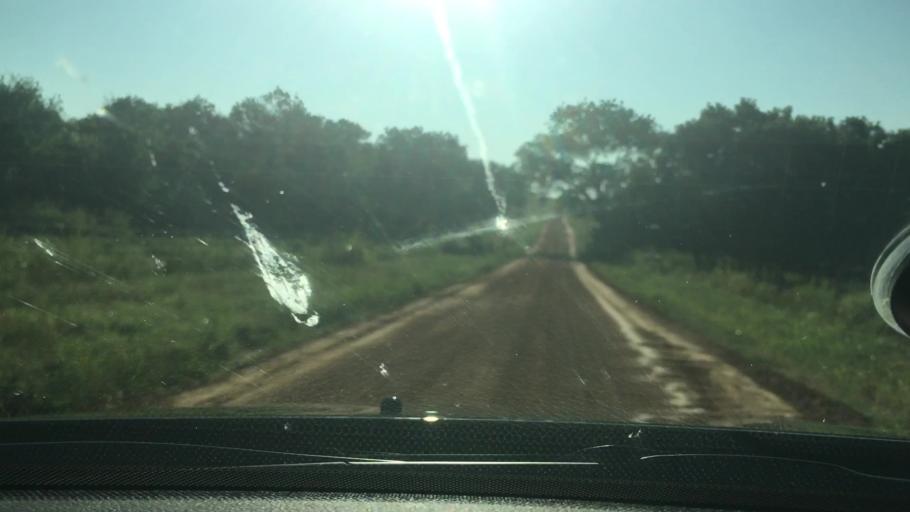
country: US
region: Oklahoma
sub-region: Murray County
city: Sulphur
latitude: 34.4194
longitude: -96.7827
